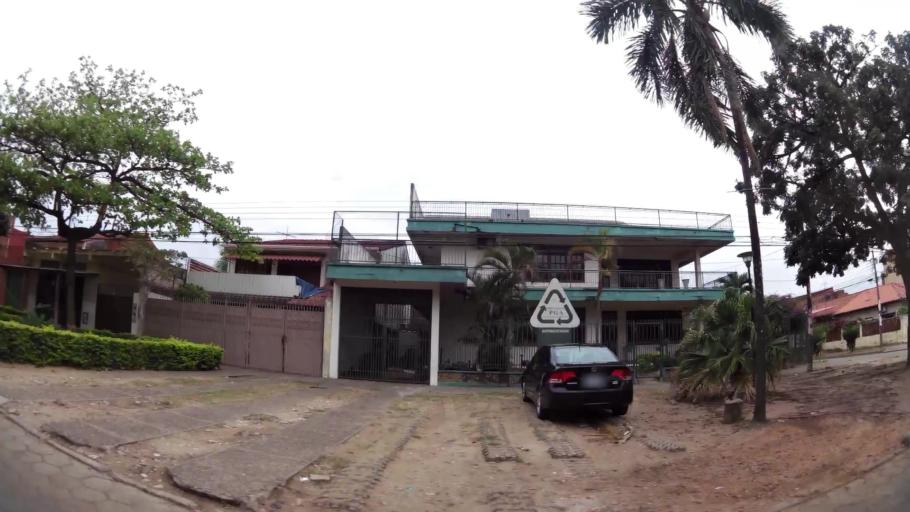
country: BO
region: Santa Cruz
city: Santa Cruz de la Sierra
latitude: -17.7984
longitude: -63.1889
